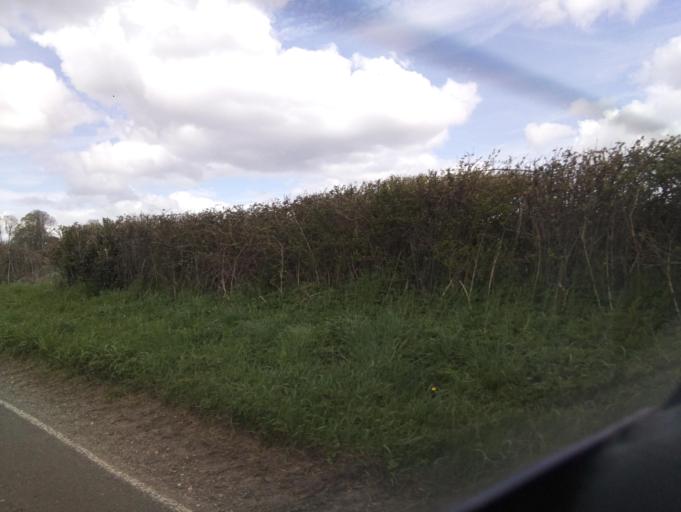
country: GB
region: England
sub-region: Hampshire
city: Andover
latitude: 51.2351
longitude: -1.4754
